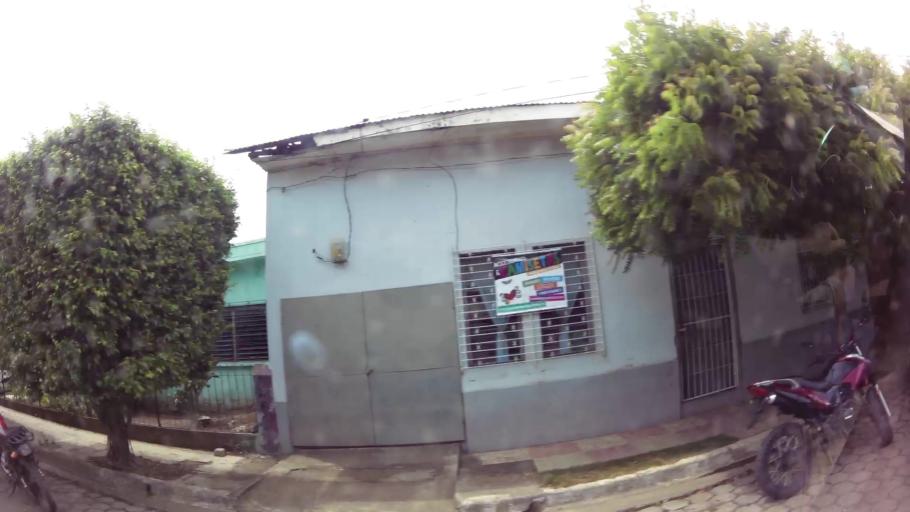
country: NI
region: Rivas
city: Rivas
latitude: 11.4364
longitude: -85.8327
